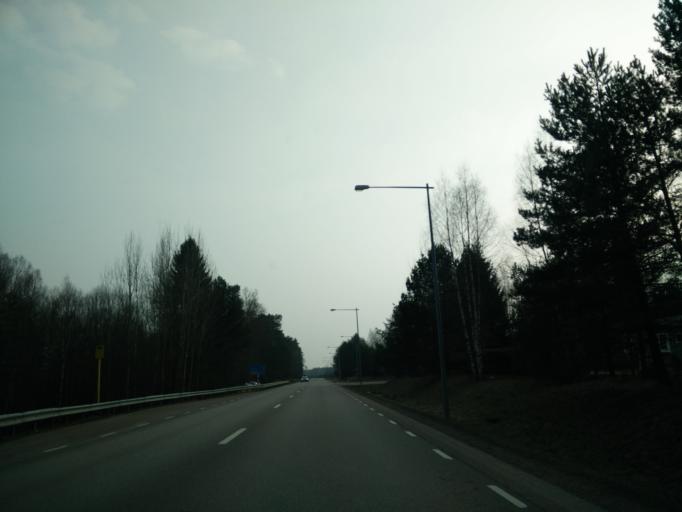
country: SE
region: Vaermland
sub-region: Forshaga Kommun
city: Forshaga
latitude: 59.5131
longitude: 13.4406
